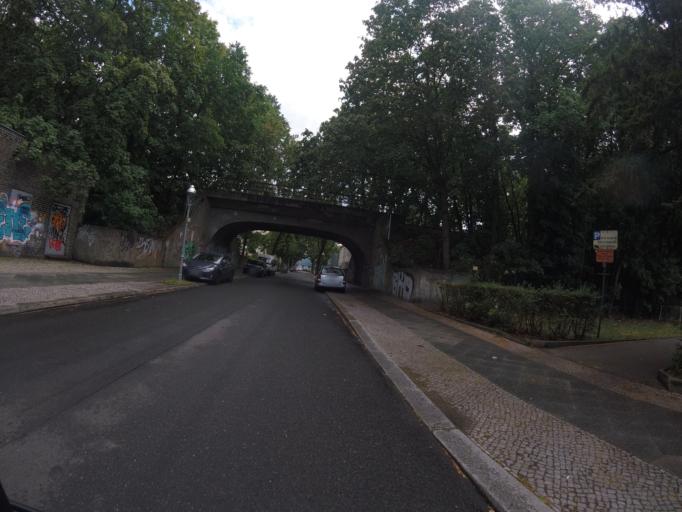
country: DE
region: Berlin
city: Siemensstadt
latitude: 52.5391
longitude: 13.2672
